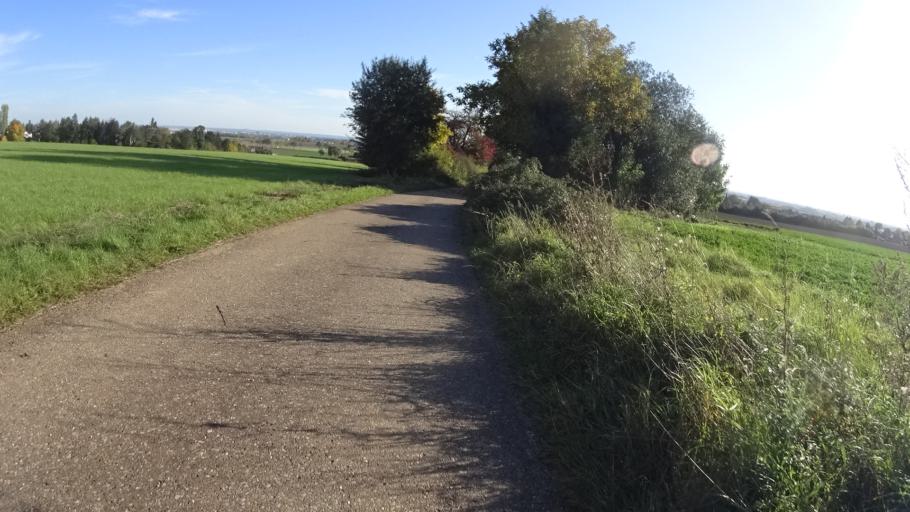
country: DE
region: Bavaria
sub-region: Upper Bavaria
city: Bohmfeld
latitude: 48.8418
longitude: 11.3618
